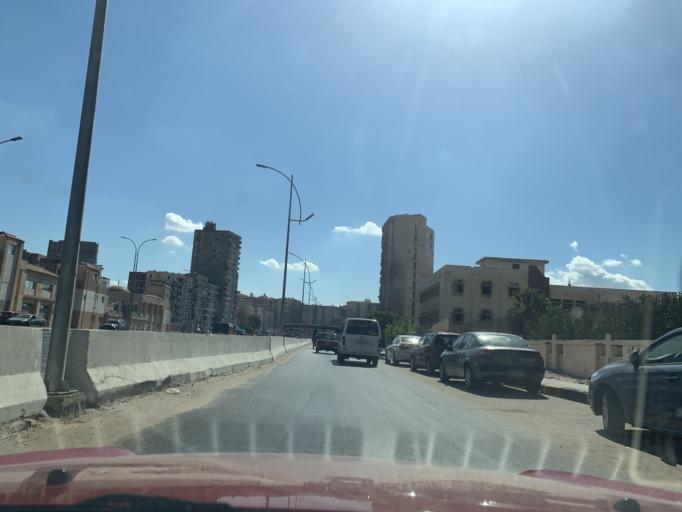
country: EG
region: Alexandria
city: Alexandria
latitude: 31.2158
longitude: 29.9626
